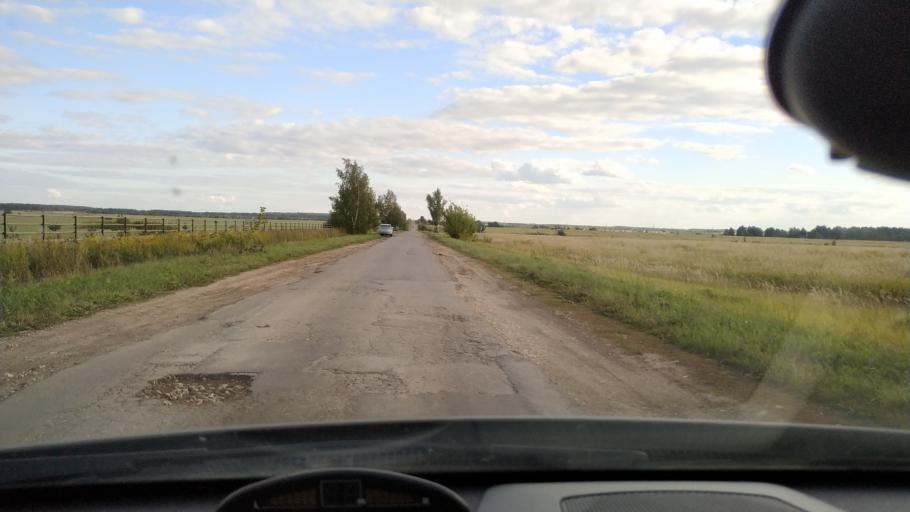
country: RU
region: Rjazan
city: Polyany
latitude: 54.5766
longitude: 39.8609
